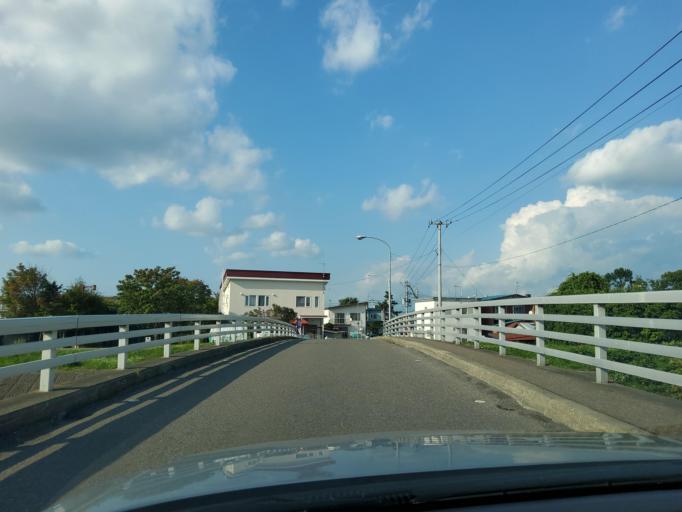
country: JP
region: Hokkaido
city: Obihiro
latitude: 42.8948
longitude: 143.1976
